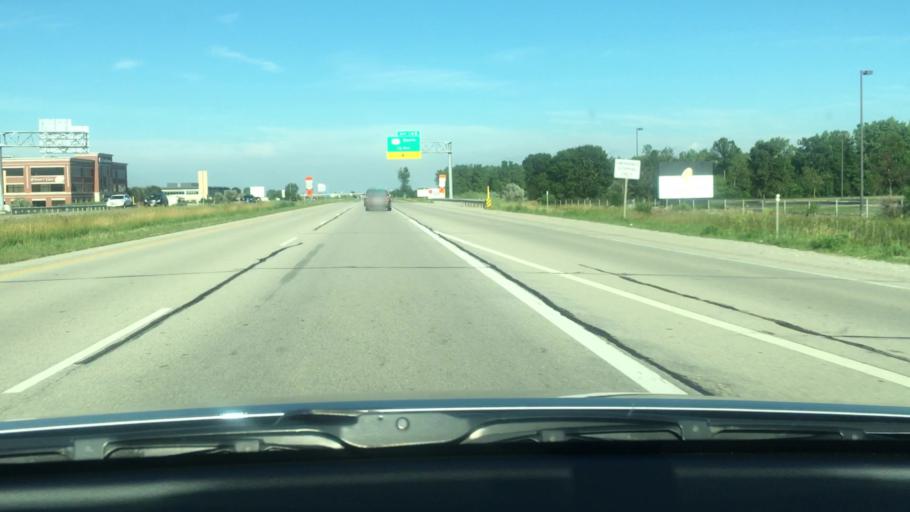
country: US
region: Wisconsin
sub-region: Outagamie County
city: Kimberly
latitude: 44.2980
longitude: -88.3714
